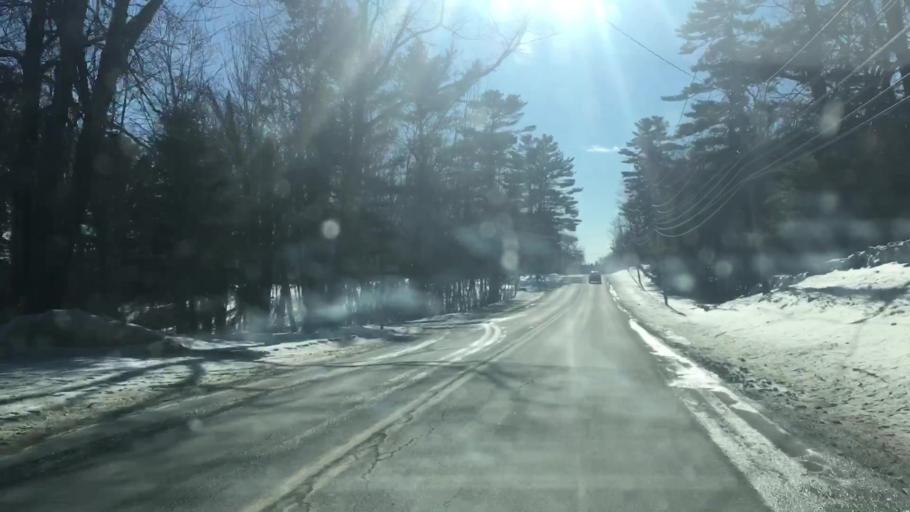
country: US
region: Maine
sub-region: Hancock County
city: Ellsworth
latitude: 44.5364
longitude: -68.4307
